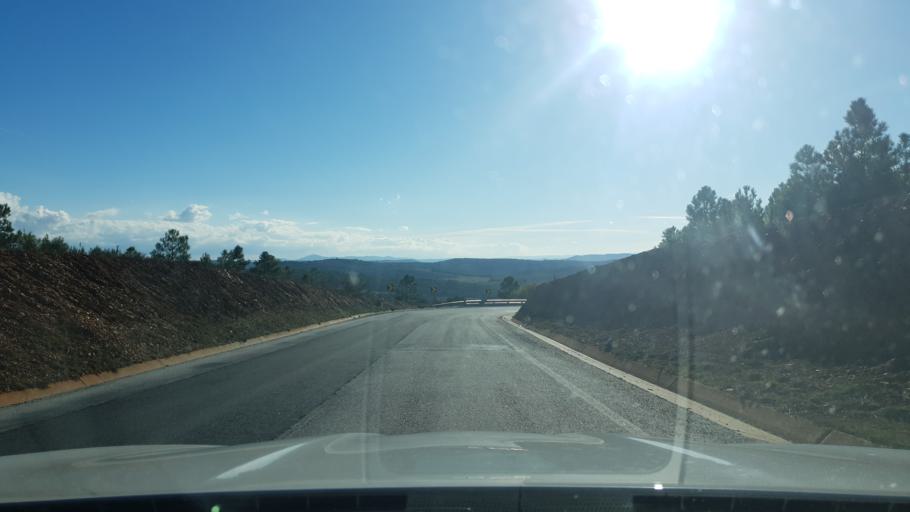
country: PT
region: Braganca
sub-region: Freixo de Espada A Cinta
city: Freixo de Espada a Cinta
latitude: 41.1309
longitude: -6.8152
